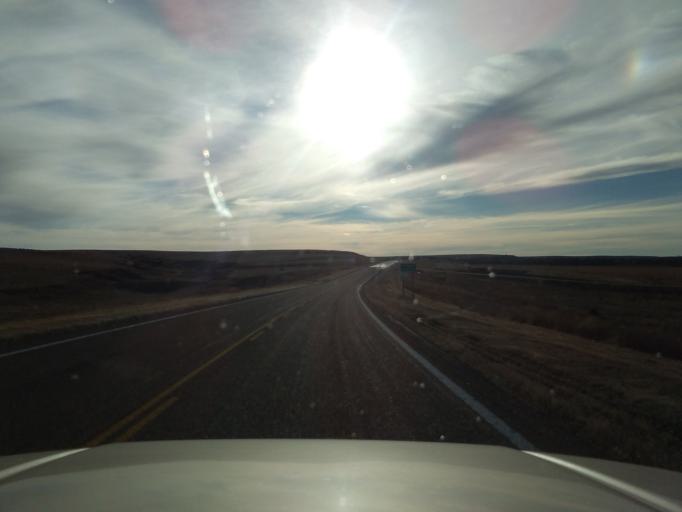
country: US
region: Kansas
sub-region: Norton County
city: Norton
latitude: 39.7323
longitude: -100.1780
